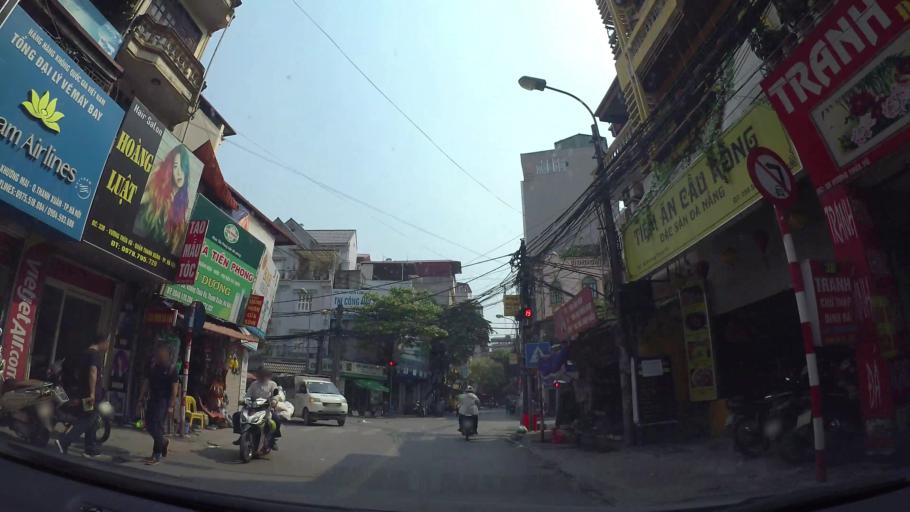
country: VN
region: Ha Noi
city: Dong Da
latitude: 21.0006
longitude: 105.8223
